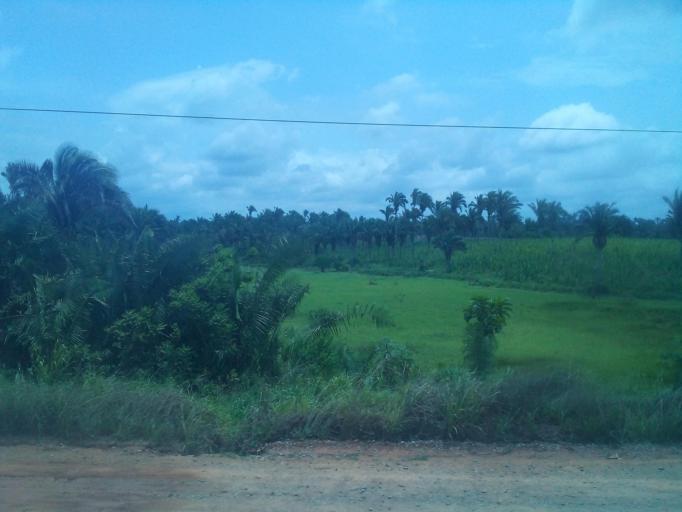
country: BR
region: Maranhao
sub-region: Santa Ines
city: Santa Ines
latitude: -3.6963
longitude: -45.6159
